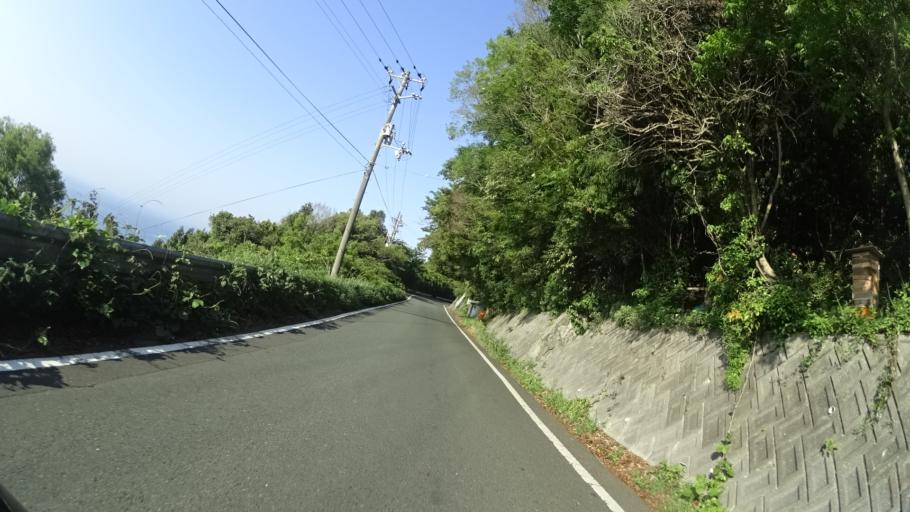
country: JP
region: Ehime
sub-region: Nishiuwa-gun
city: Ikata-cho
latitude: 33.3842
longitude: 132.0864
